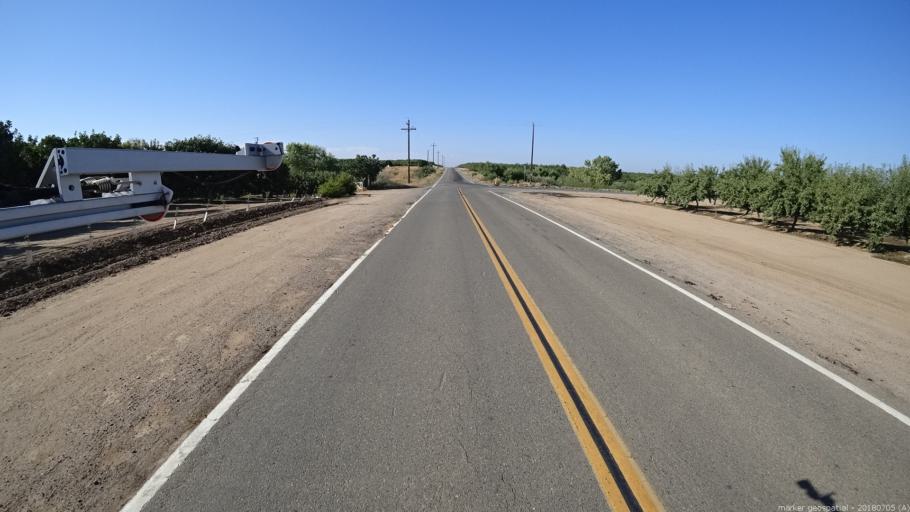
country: US
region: California
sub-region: Madera County
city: Madera Acres
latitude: 37.0984
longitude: -120.0746
